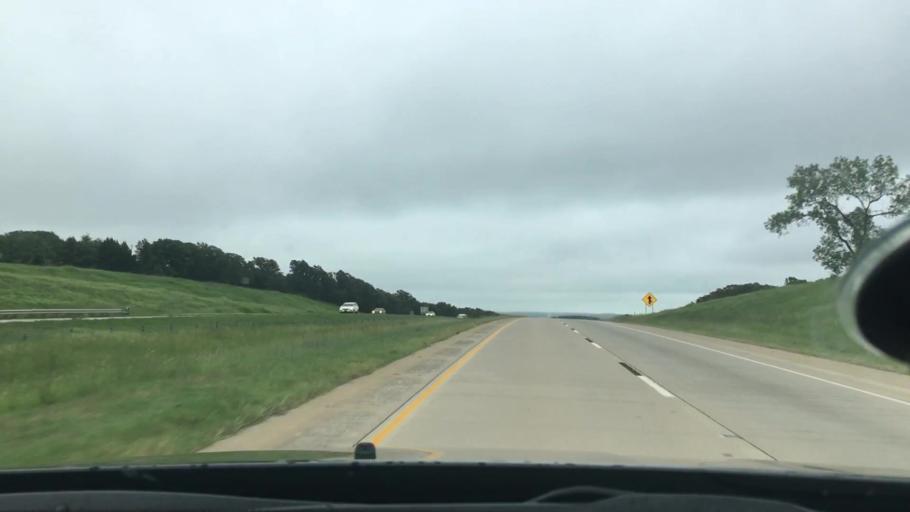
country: US
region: Oklahoma
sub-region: Okfuskee County
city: Okemah
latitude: 35.4303
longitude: -96.1934
